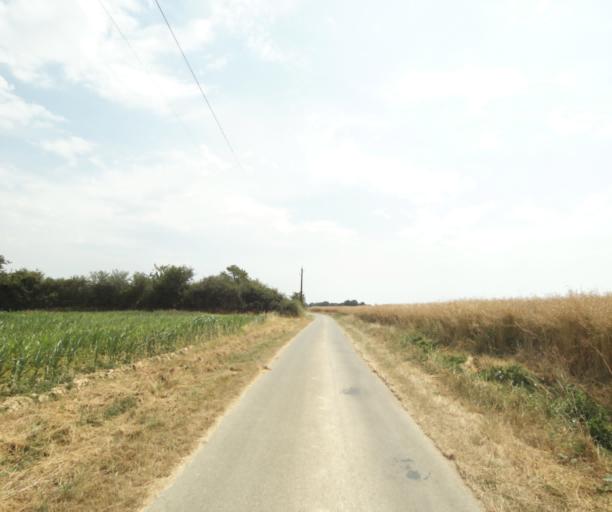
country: FR
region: Centre
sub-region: Departement d'Eure-et-Loir
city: La Bazoche-Gouet
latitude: 48.1834
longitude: 1.0009
